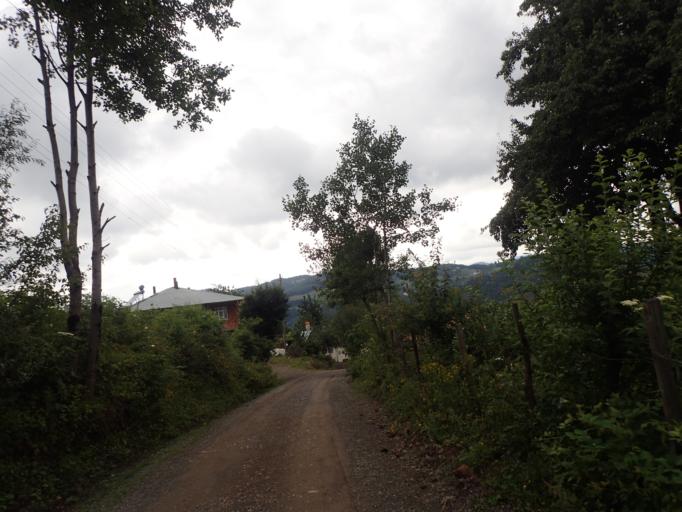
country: TR
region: Ordu
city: Akkus
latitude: 40.8180
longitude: 37.0899
